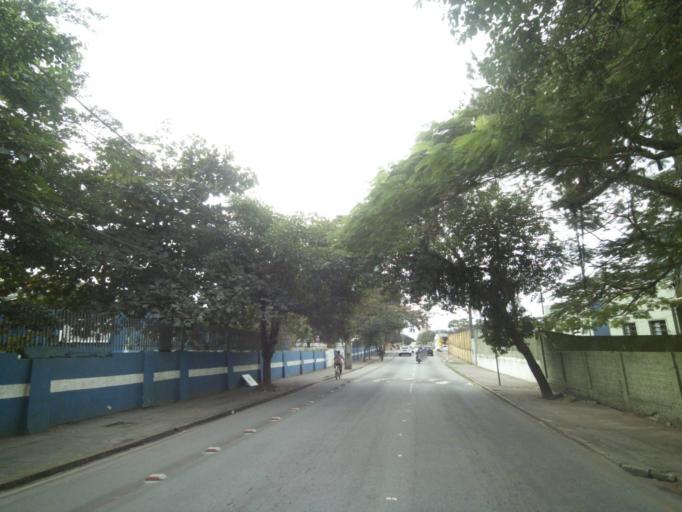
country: BR
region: Parana
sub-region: Paranagua
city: Paranagua
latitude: -25.5226
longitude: -48.5124
